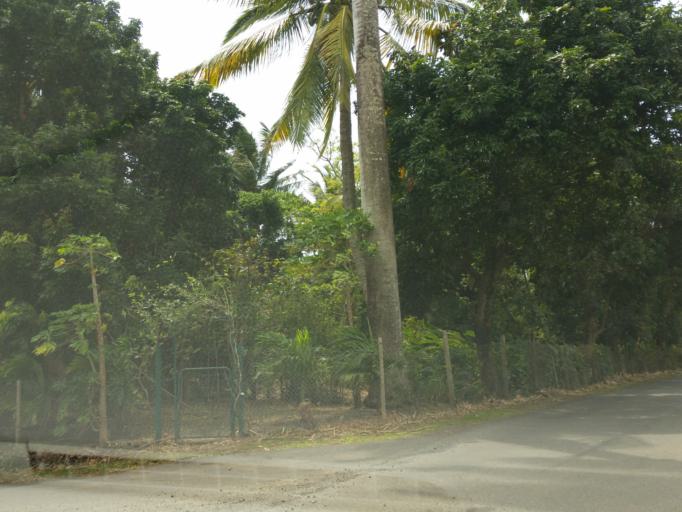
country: RE
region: Reunion
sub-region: Reunion
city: Sainte-Suzanne
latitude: -20.9171
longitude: 55.6133
